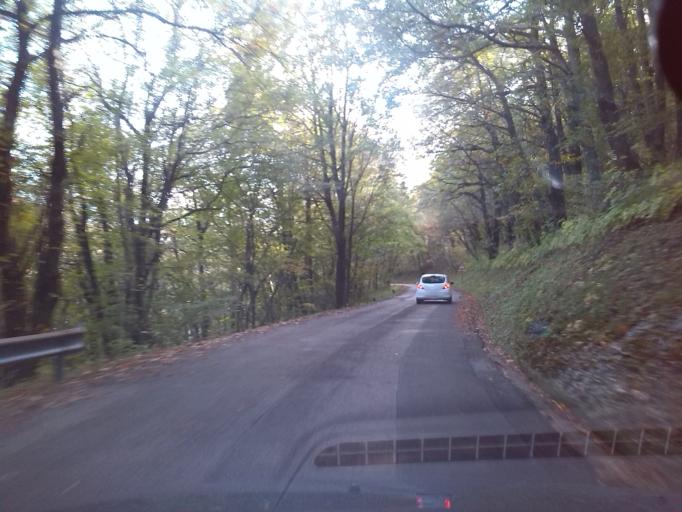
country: IT
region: Friuli Venezia Giulia
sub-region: Provincia di Udine
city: Stregna
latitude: 46.1279
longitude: 13.6062
